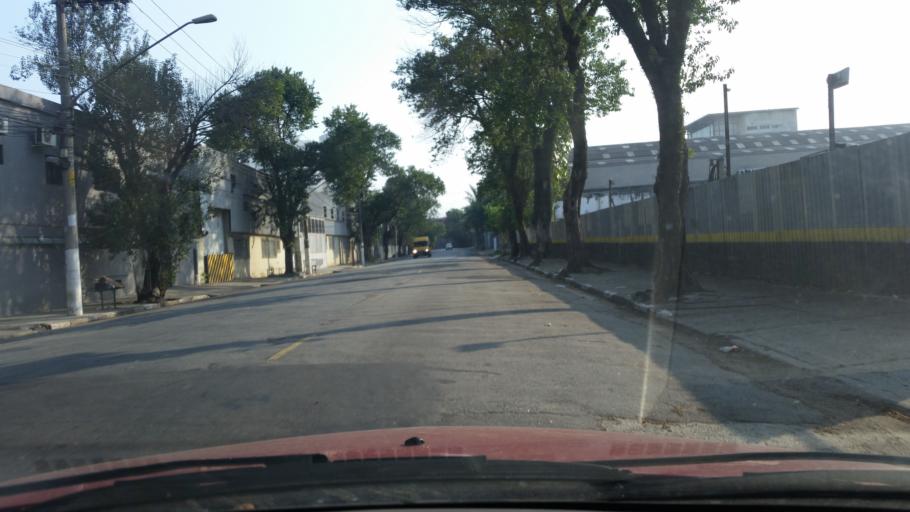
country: BR
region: Sao Paulo
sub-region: Osasco
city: Osasco
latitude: -23.5287
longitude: -46.7422
